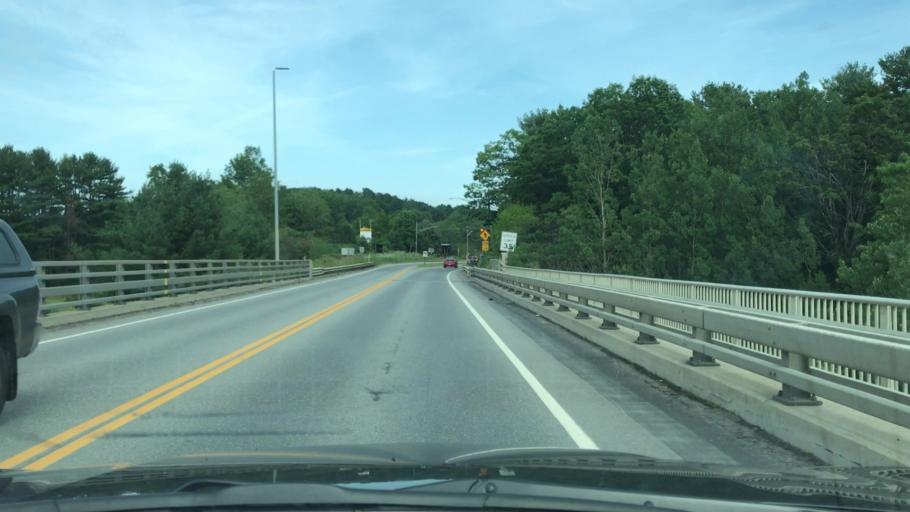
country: US
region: Maine
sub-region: Waldo County
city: Belfast
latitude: 44.4339
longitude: -69.0078
